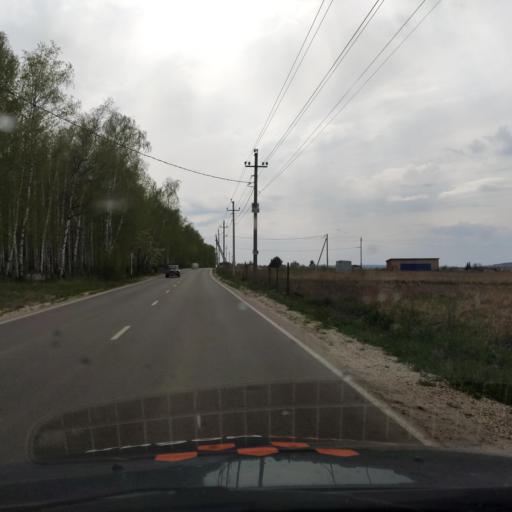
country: RU
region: Voronezj
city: Podgornoye
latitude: 51.8445
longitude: 39.1456
